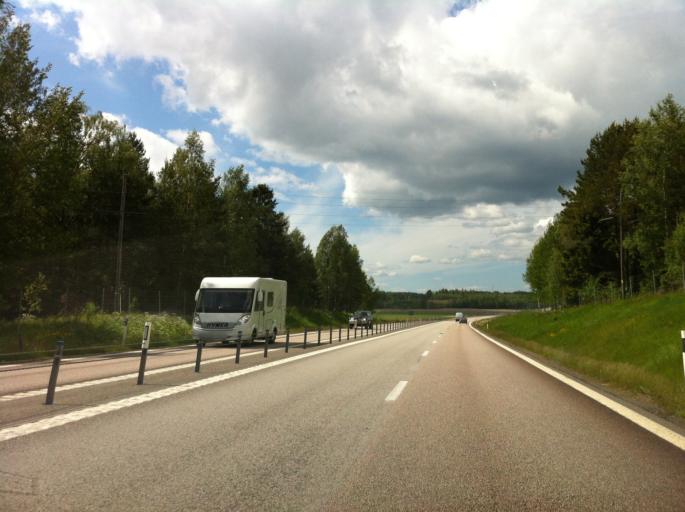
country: SE
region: Vaermland
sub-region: Saffle Kommun
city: Saeffle
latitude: 59.1216
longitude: 12.8560
